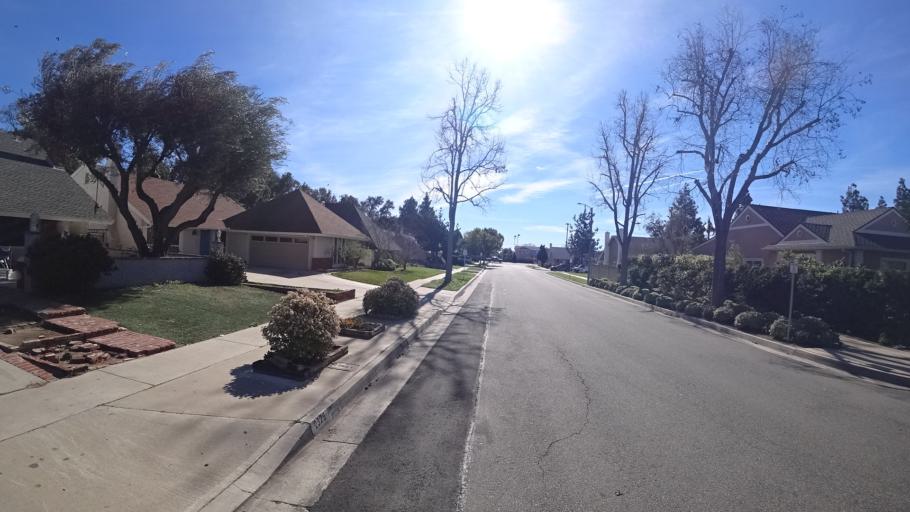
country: US
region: California
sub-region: Orange County
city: Orange
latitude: 33.7683
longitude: -117.8449
